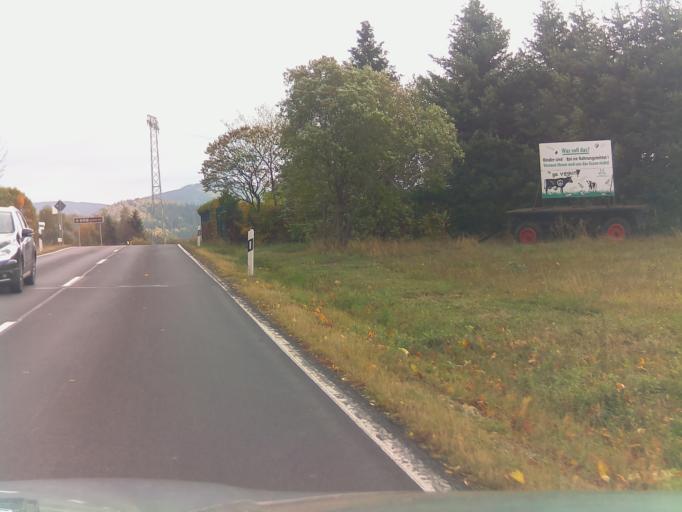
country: DE
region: Thuringia
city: Rotterode
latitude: 50.7146
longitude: 10.5445
